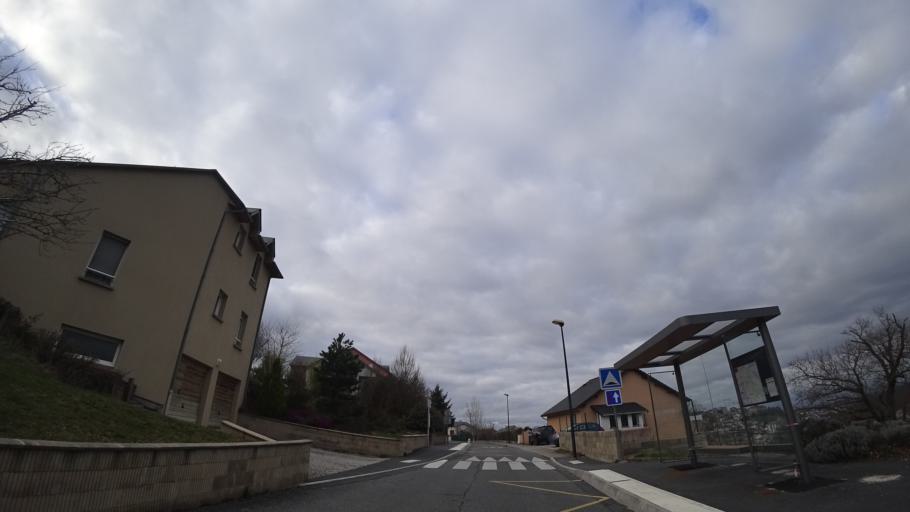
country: FR
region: Midi-Pyrenees
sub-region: Departement de l'Aveyron
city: Le Monastere
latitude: 44.3364
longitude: 2.5731
